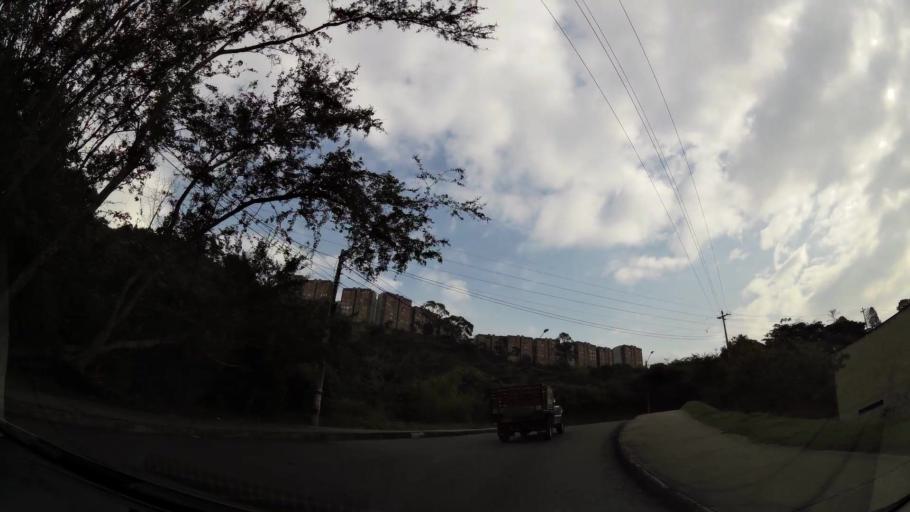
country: CO
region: Antioquia
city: Medellin
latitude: 6.2840
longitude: -75.5978
